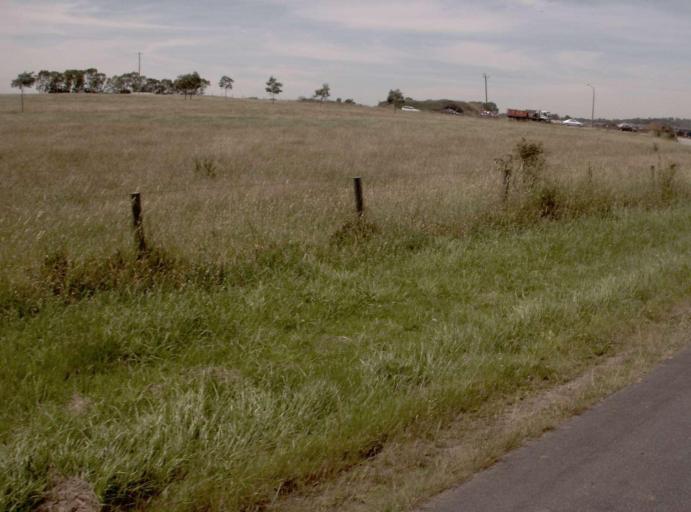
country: AU
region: Victoria
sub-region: Frankston
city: Skye
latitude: -38.1056
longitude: 145.2340
